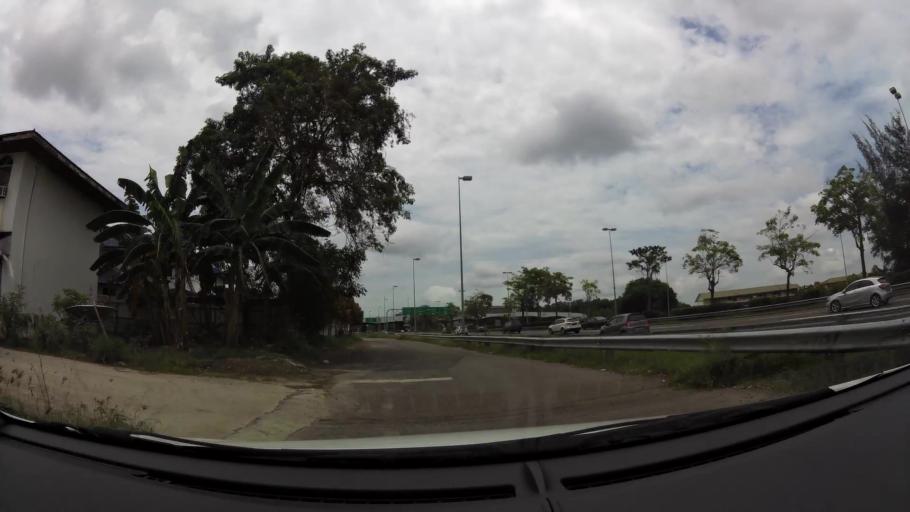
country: BN
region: Brunei and Muara
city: Bandar Seri Begawan
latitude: 4.9128
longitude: 114.9210
